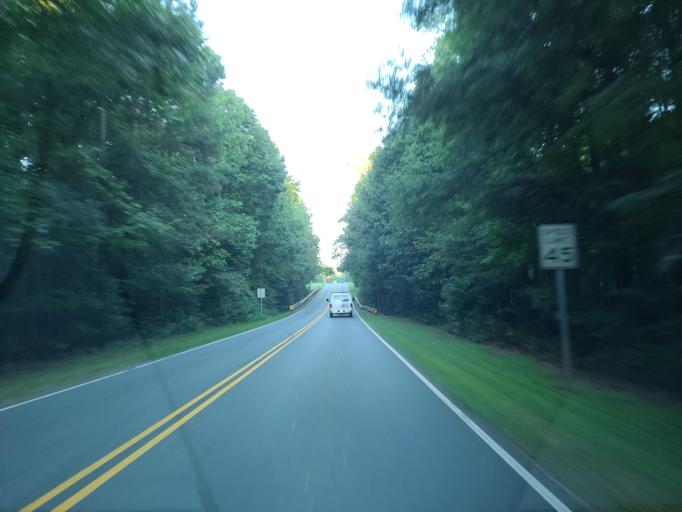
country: US
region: North Carolina
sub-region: Union County
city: Weddington
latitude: 35.0142
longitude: -80.7468
